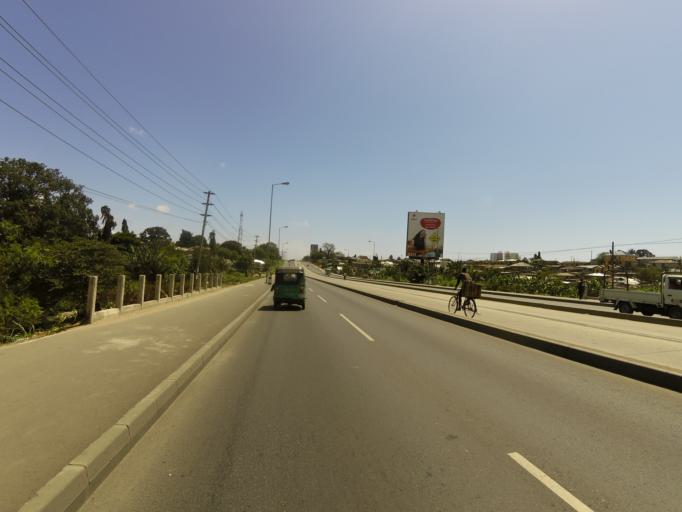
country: TZ
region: Dar es Salaam
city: Magomeni
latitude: -6.8011
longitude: 39.2621
